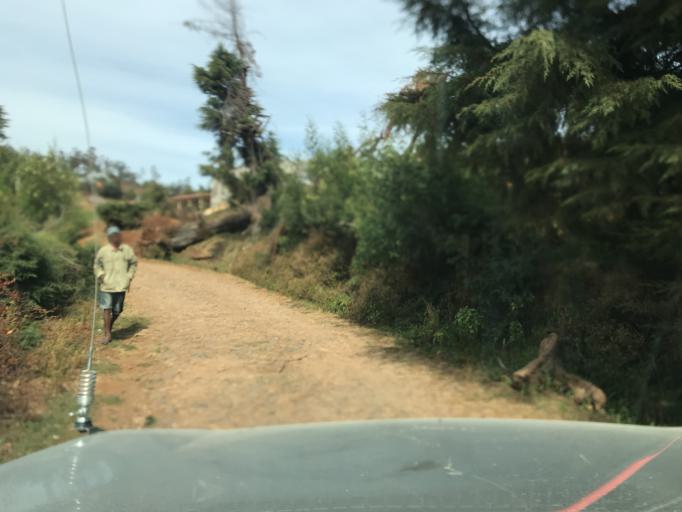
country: TL
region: Ainaro
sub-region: Ainaro
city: Ainaro
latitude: -8.8832
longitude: 125.5376
